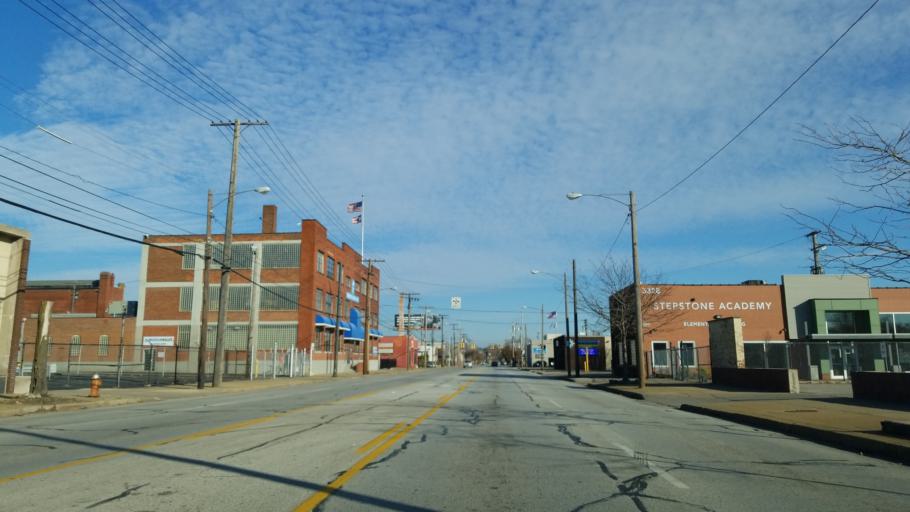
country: US
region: Ohio
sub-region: Cuyahoga County
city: Cleveland
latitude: 41.5002
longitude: -81.6645
